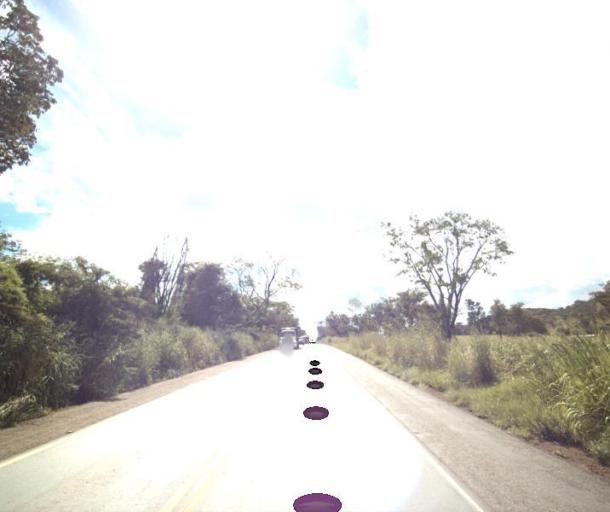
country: BR
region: Goias
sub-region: Jaragua
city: Jaragua
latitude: -15.9264
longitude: -49.2114
